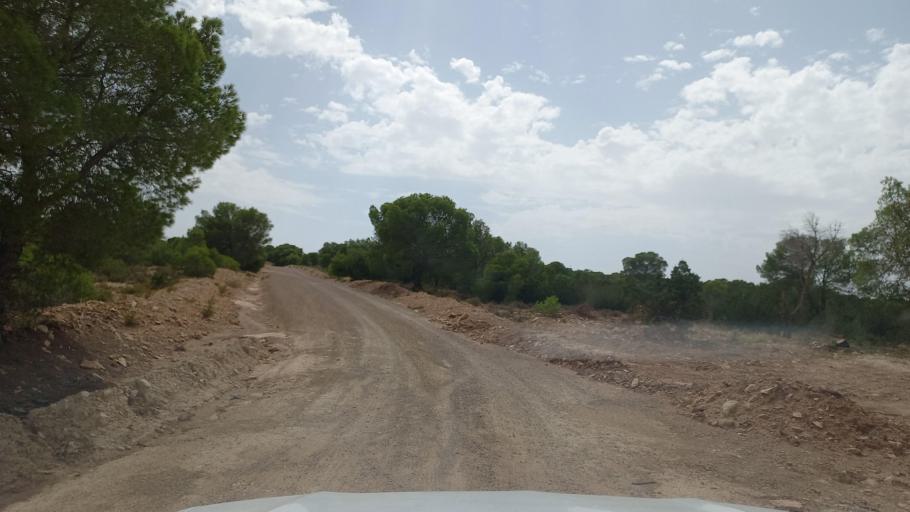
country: TN
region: Al Qasrayn
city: Kasserine
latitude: 35.3825
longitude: 8.8808
